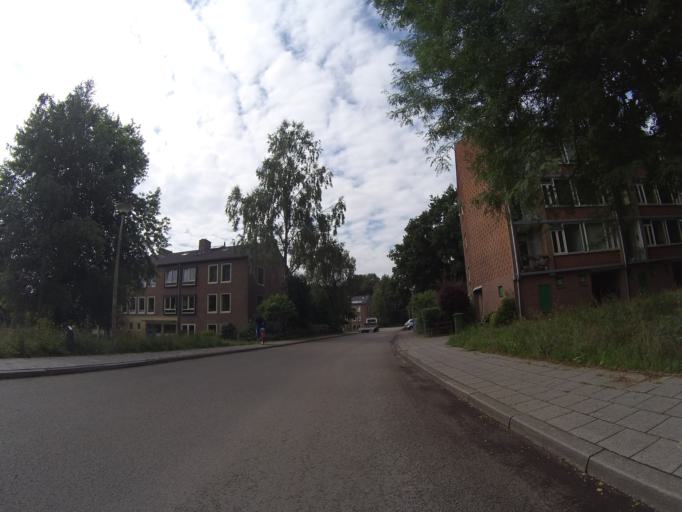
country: NL
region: Utrecht
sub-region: Gemeente Amersfoort
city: Amersfoort
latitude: 52.1397
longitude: 5.3709
